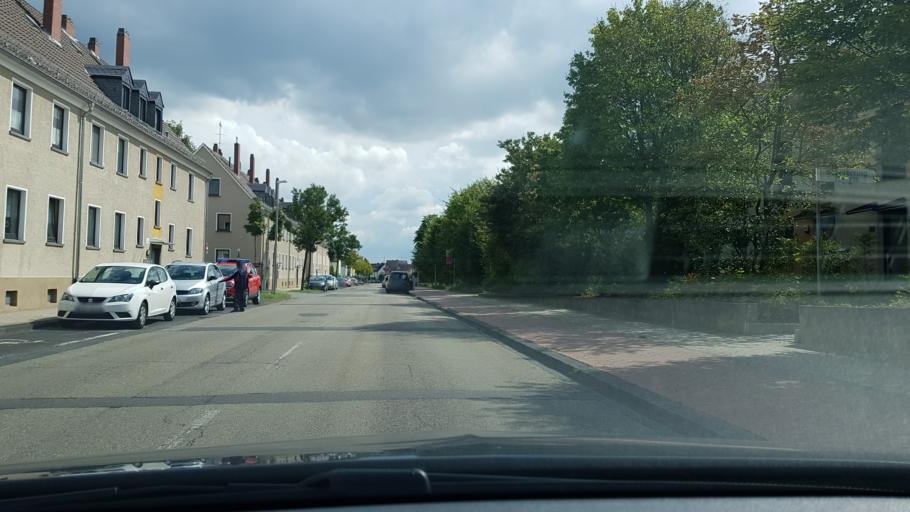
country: DE
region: Rheinland-Pfalz
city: Andernach
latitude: 50.4257
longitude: 7.4073
